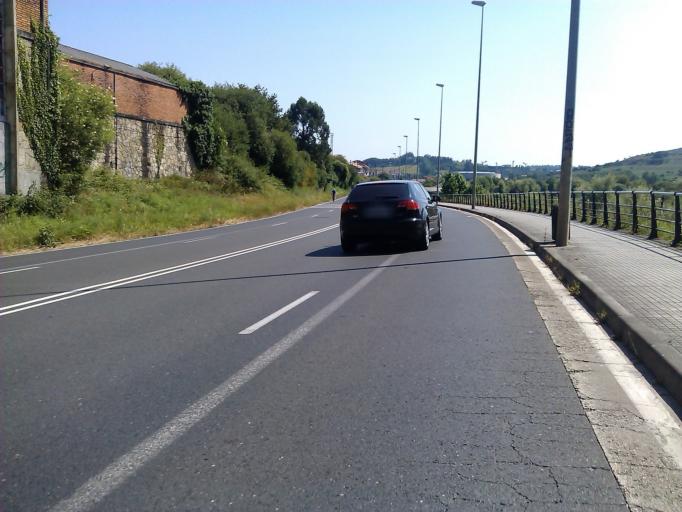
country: ES
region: Galicia
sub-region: Provincia da Coruna
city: Santiago de Compostela
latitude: 42.8698
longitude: -8.5435
